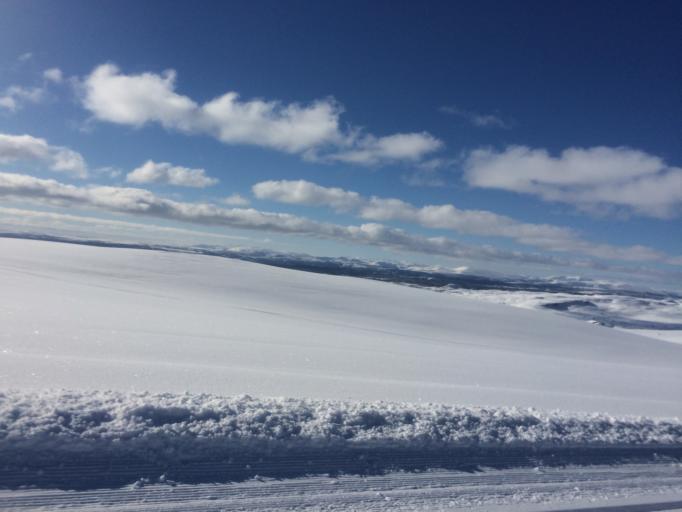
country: NO
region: Oppland
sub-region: Ringebu
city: Ringebu
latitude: 61.3578
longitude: 10.0852
